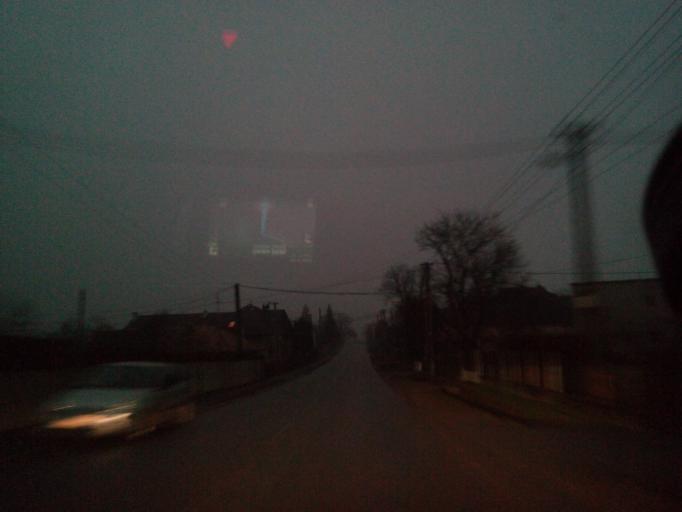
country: SK
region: Presovsky
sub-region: Okres Presov
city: Presov
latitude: 49.0146
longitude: 21.1864
